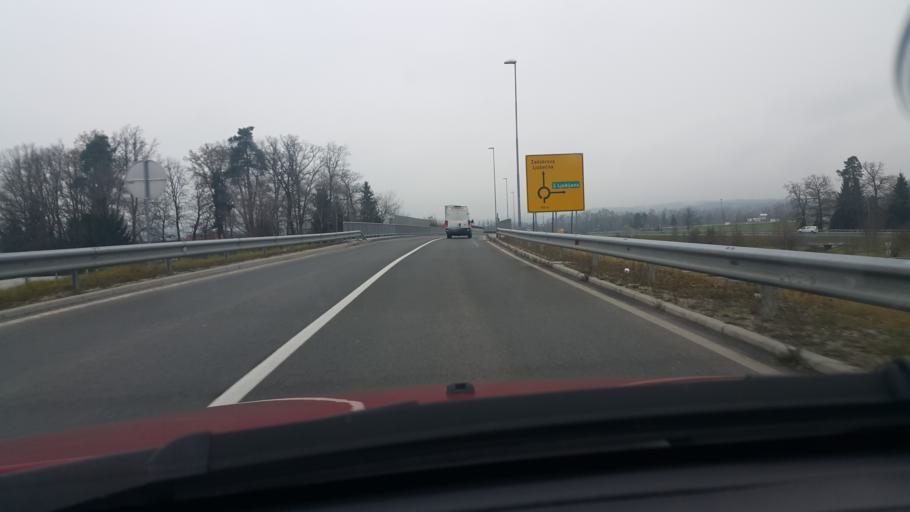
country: SI
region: Celje
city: Ljubecna
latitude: 46.2536
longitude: 15.3106
